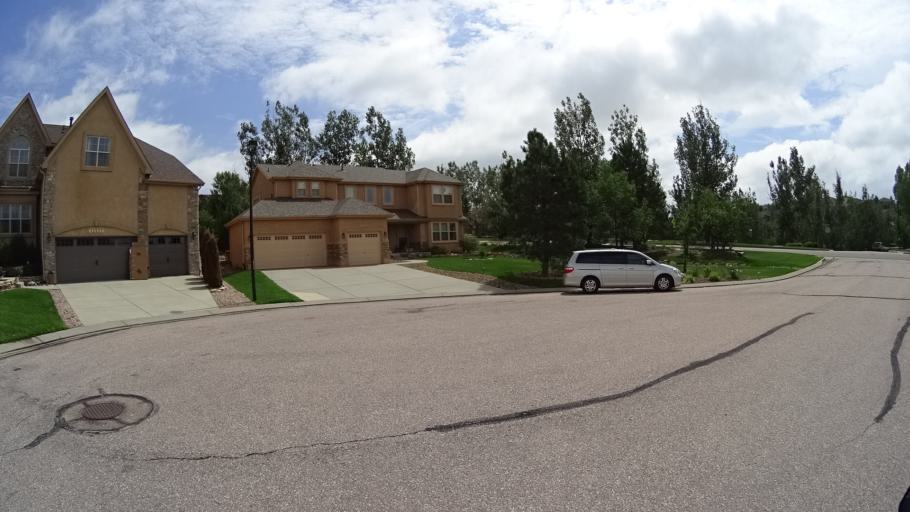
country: US
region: Colorado
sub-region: El Paso County
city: Gleneagle
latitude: 39.0139
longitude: -104.8003
